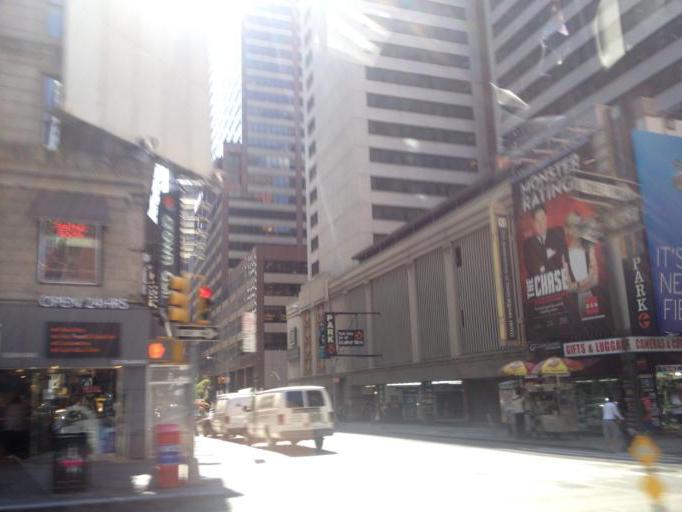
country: US
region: New York
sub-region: New York County
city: Manhattan
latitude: 40.7628
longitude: -73.9832
